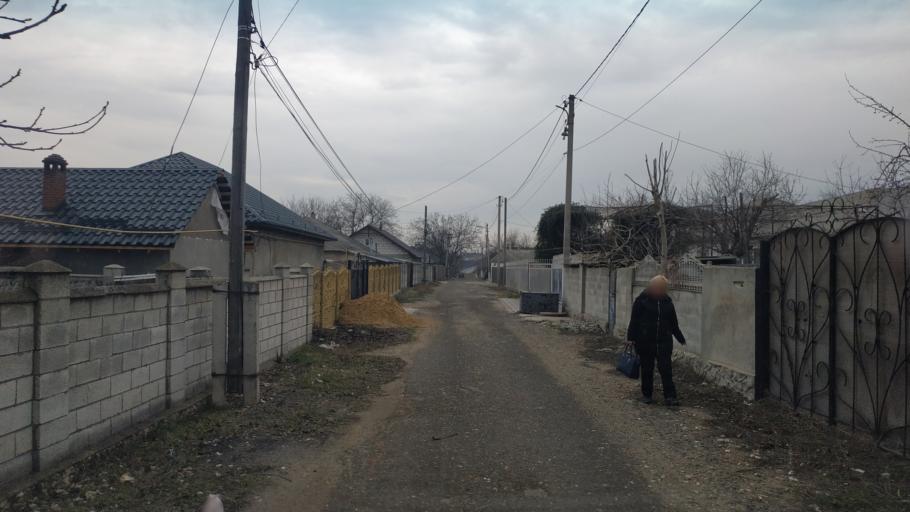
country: MD
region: Chisinau
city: Singera
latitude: 46.9187
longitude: 28.9643
